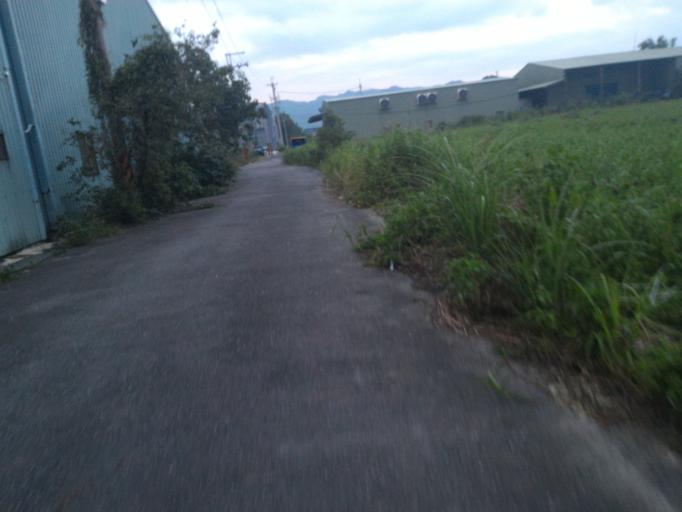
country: TW
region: Taiwan
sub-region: Taoyuan
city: Taoyuan
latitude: 24.9521
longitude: 121.3985
